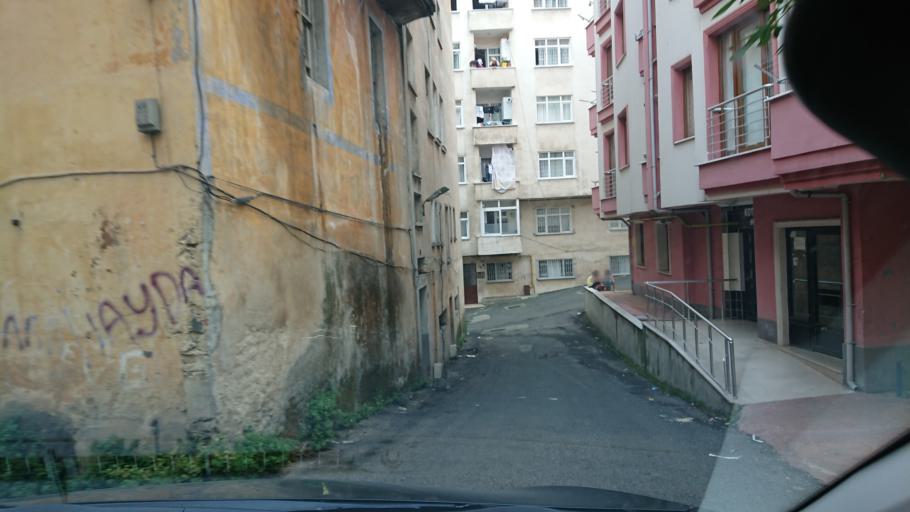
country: TR
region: Rize
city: Rize
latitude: 41.0224
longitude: 40.5177
